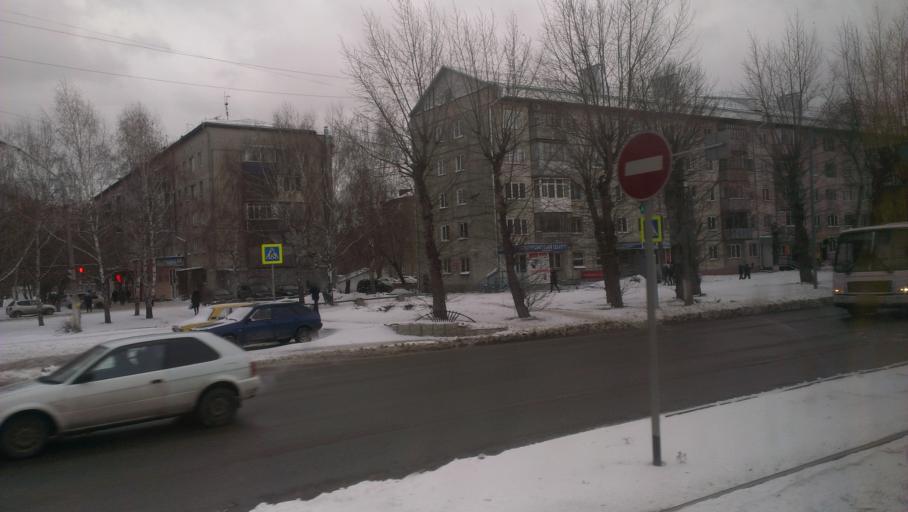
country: RU
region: Altai Krai
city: Novosilikatnyy
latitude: 53.3666
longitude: 83.6767
